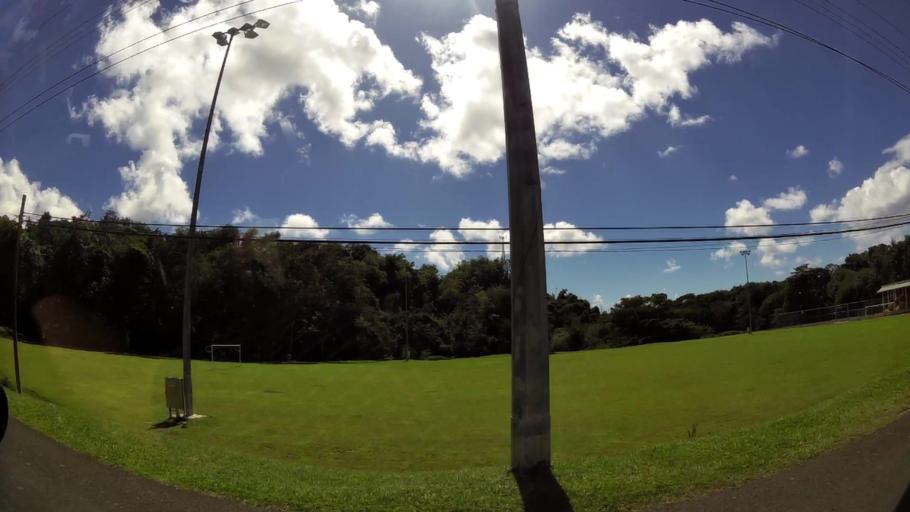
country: TT
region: Tobago
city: Scarborough
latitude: 11.2258
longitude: -60.7499
